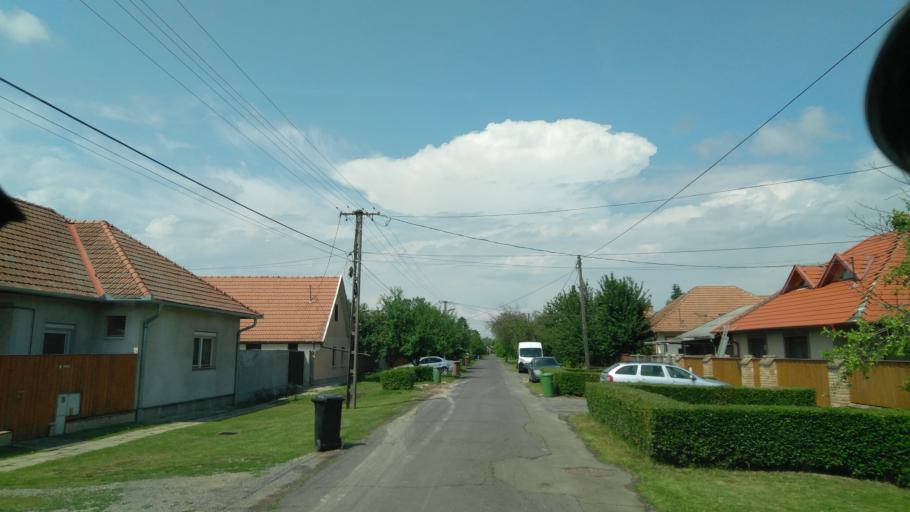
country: HU
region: Bekes
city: Bekes
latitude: 46.7592
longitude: 21.1469
